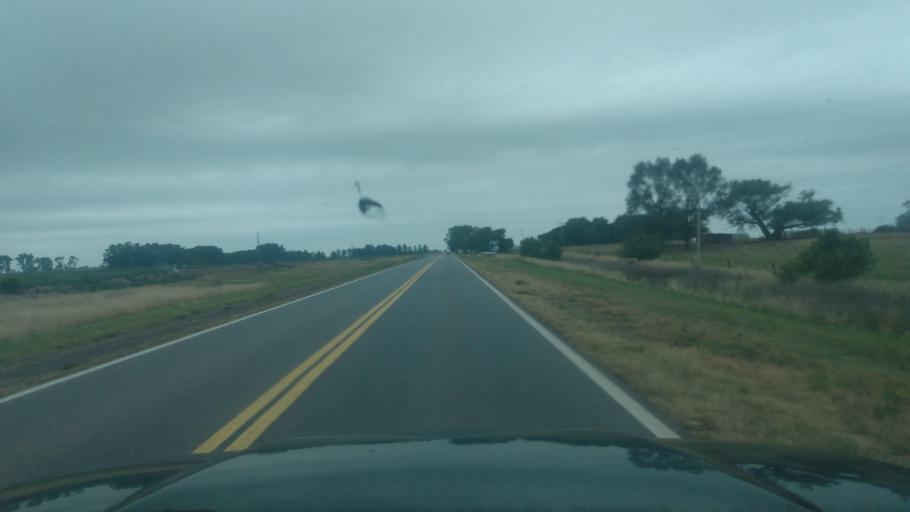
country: AR
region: Buenos Aires
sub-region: Partido de Bragado
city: Bragado
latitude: -35.2778
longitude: -60.5883
